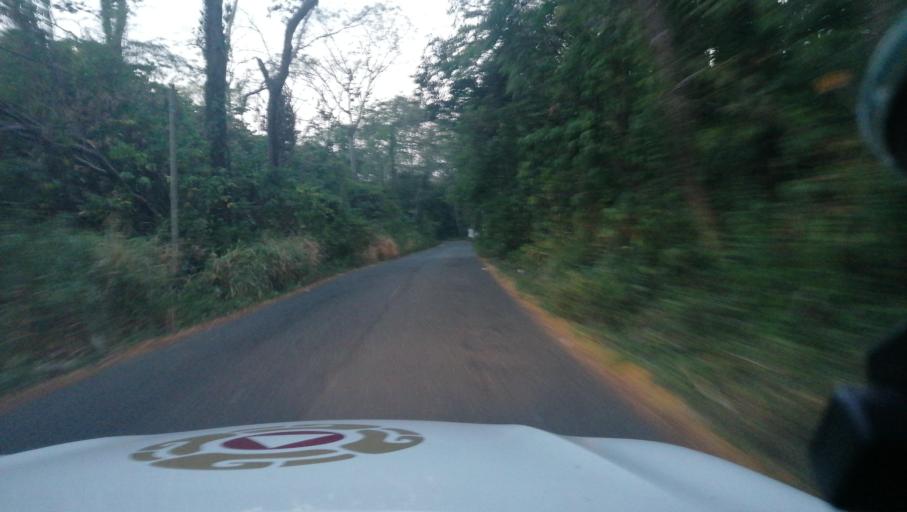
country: MX
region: Chiapas
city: Veinte de Noviembre
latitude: 15.0150
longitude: -92.2459
